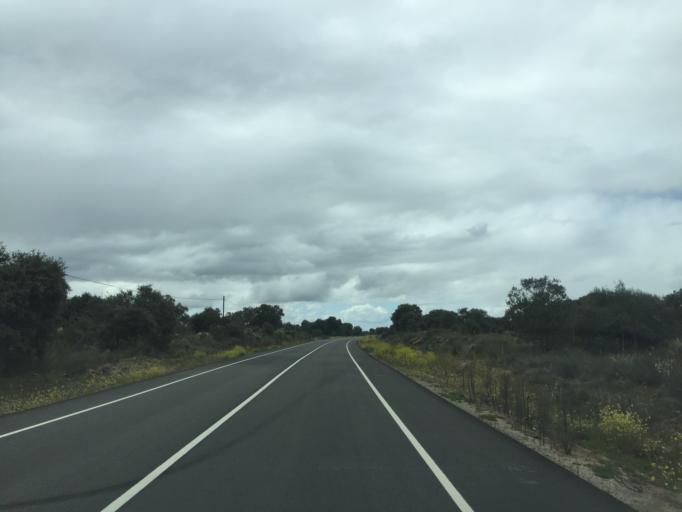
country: ES
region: Castille and Leon
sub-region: Provincia de Zamora
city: Torregamones
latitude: 41.4751
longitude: -6.2087
